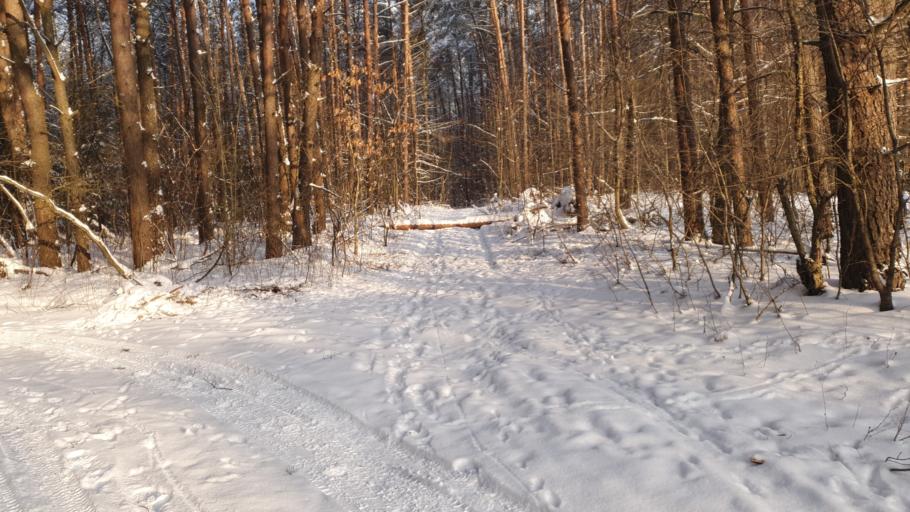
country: LT
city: Skaidiskes
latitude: 54.6399
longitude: 25.4153
